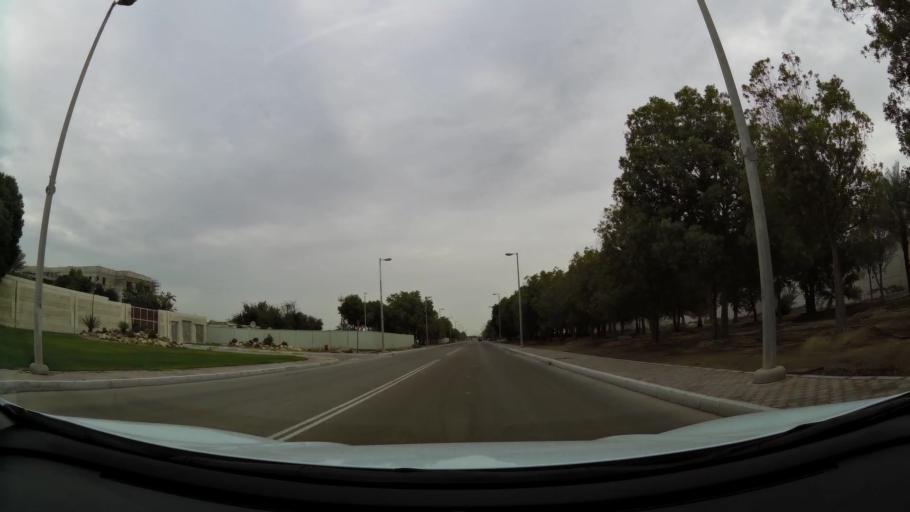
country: AE
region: Abu Dhabi
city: Abu Dhabi
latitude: 24.4117
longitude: 54.4322
